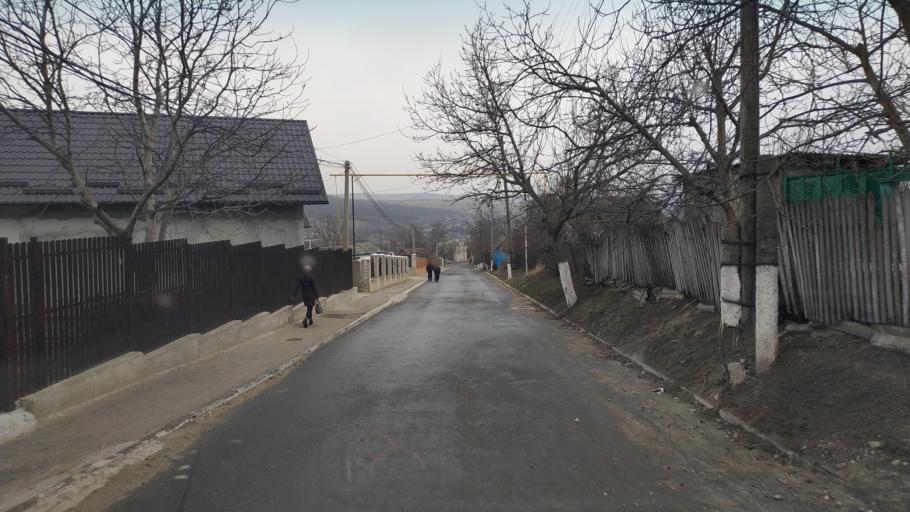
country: MD
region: Chisinau
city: Singera
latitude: 46.8300
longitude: 28.9732
